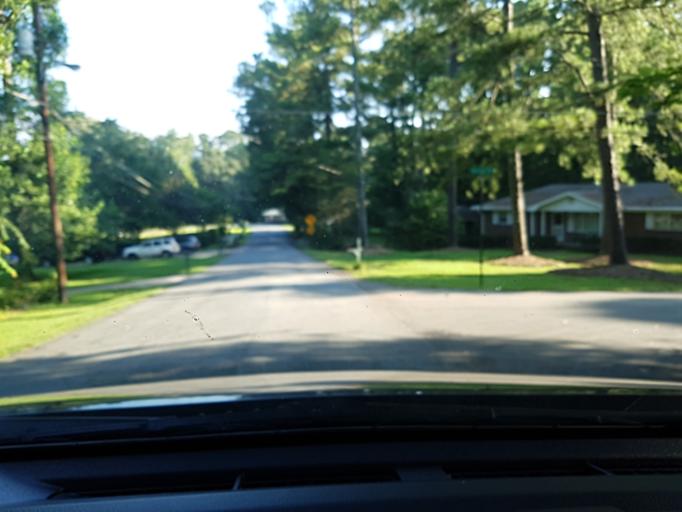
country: US
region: Georgia
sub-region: Cobb County
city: Mableton
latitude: 33.8194
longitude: -84.5886
